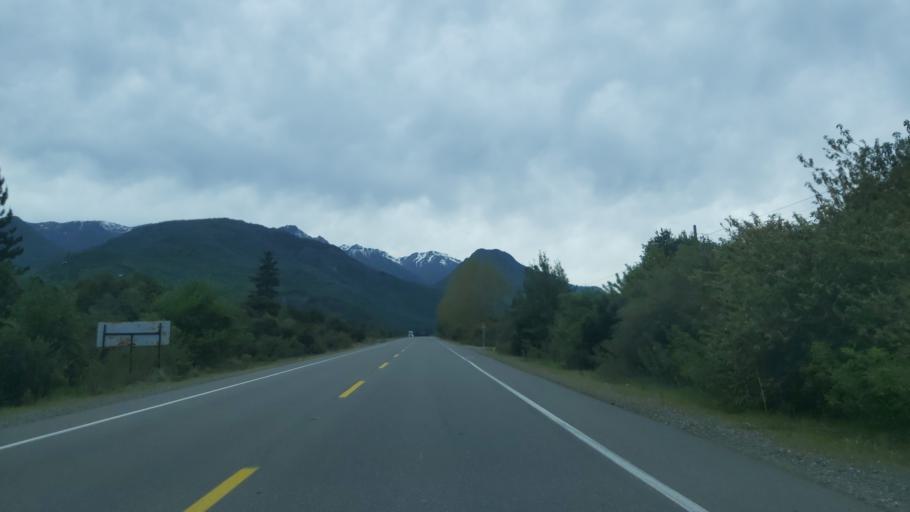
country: CL
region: Maule
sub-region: Provincia de Linares
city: Colbun
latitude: -35.7148
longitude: -71.1150
